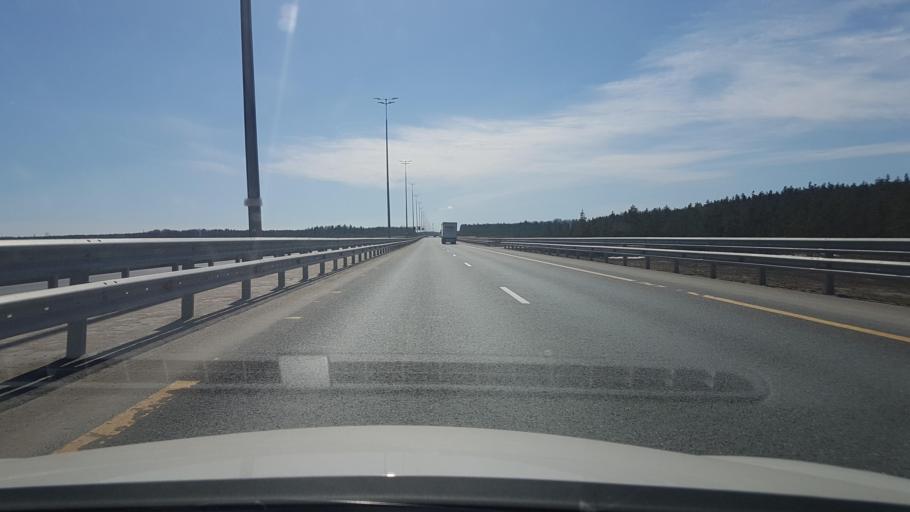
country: RU
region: Novgorod
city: Chudovo
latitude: 59.0023
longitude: 31.3611
